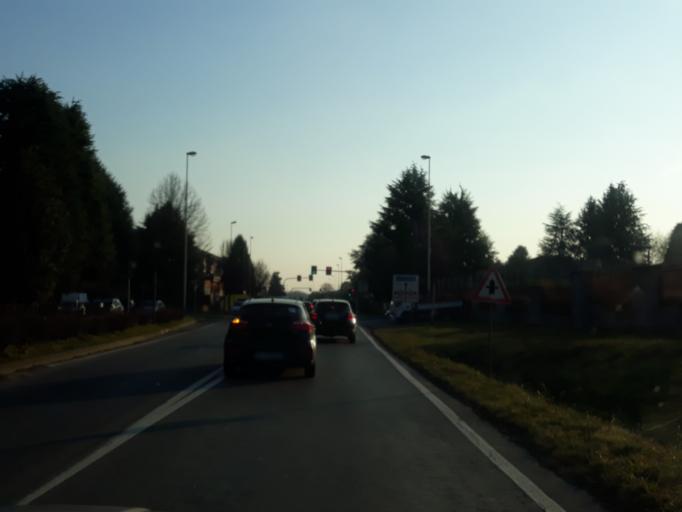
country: IT
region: Lombardy
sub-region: Provincia di Monza e Brianza
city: Bellusco
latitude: 45.6182
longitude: 9.4233
